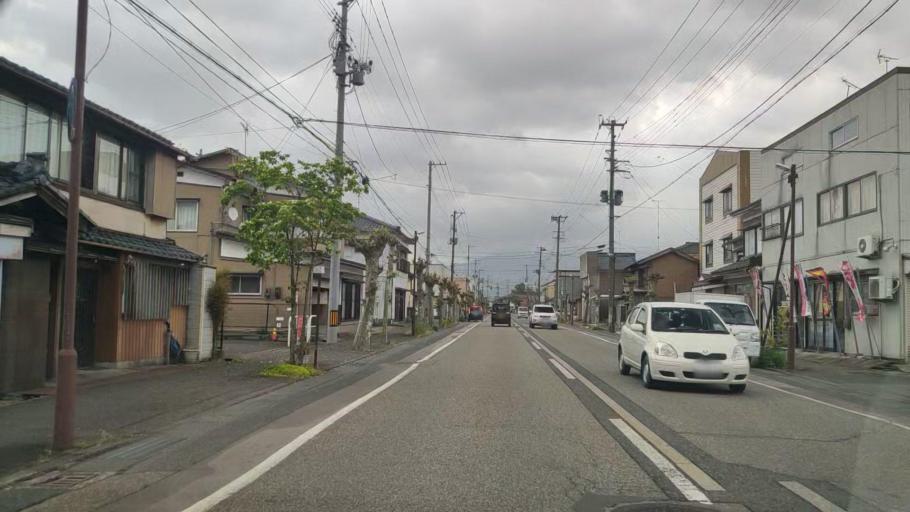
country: JP
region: Niigata
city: Gosen
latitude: 37.7373
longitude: 139.1833
